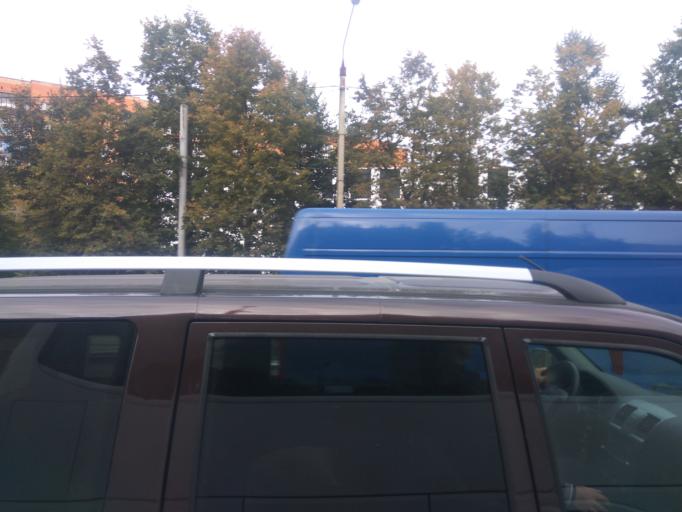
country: RU
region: Moskovskaya
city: Fryazino
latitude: 55.9514
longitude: 38.0508
